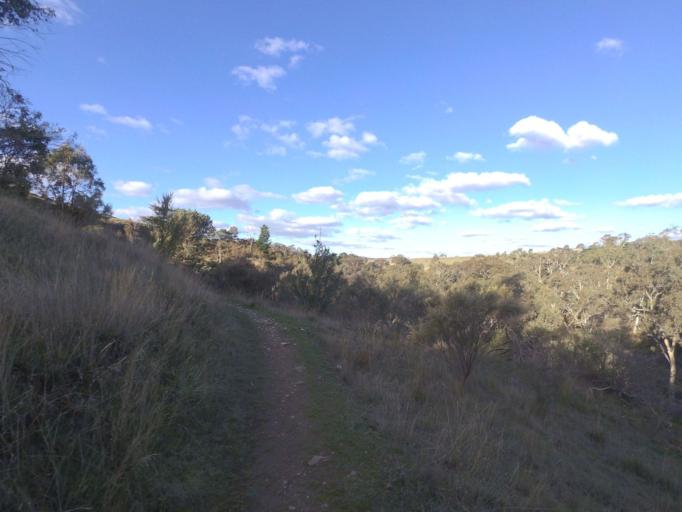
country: AU
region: Victoria
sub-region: Mount Alexander
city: Castlemaine
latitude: -37.1621
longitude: 144.2174
